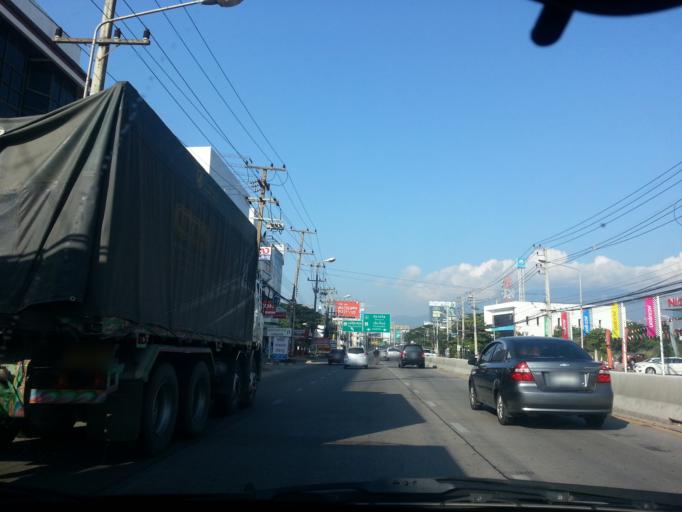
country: TH
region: Chiang Mai
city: Chiang Mai
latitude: 18.7677
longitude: 98.9827
